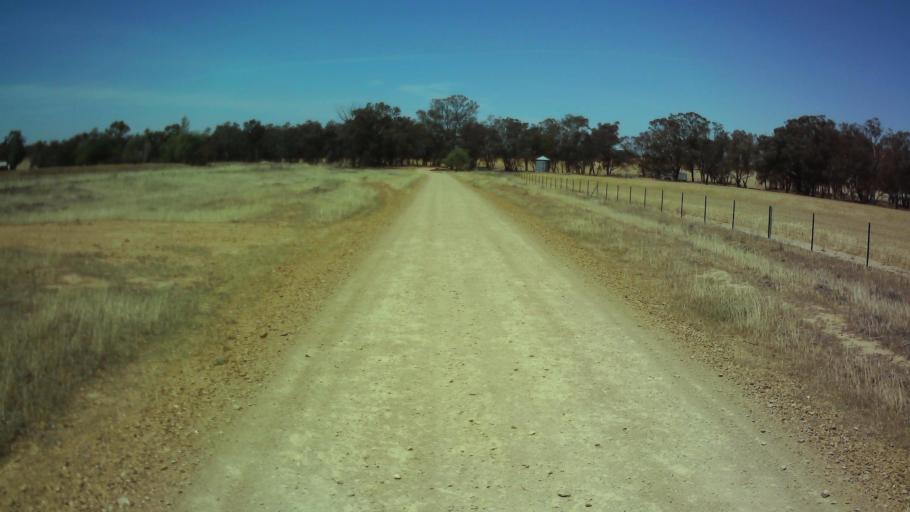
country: AU
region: New South Wales
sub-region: Weddin
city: Grenfell
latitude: -33.9235
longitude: 148.1888
